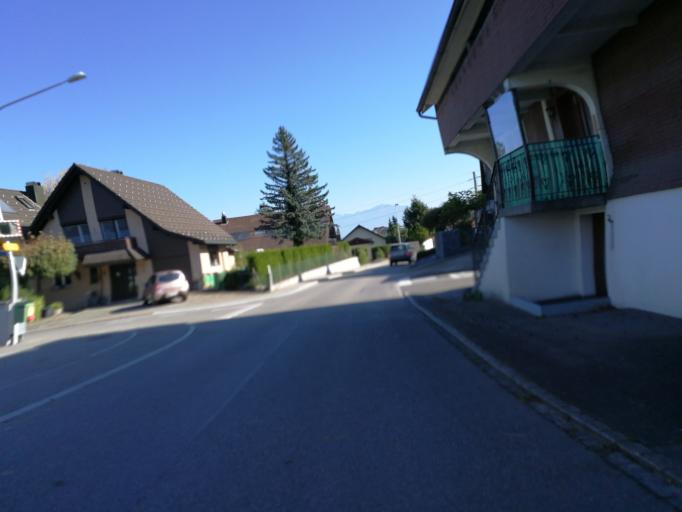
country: CH
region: Schwyz
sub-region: Bezirk March
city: Altendorf
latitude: 47.1943
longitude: 8.8070
